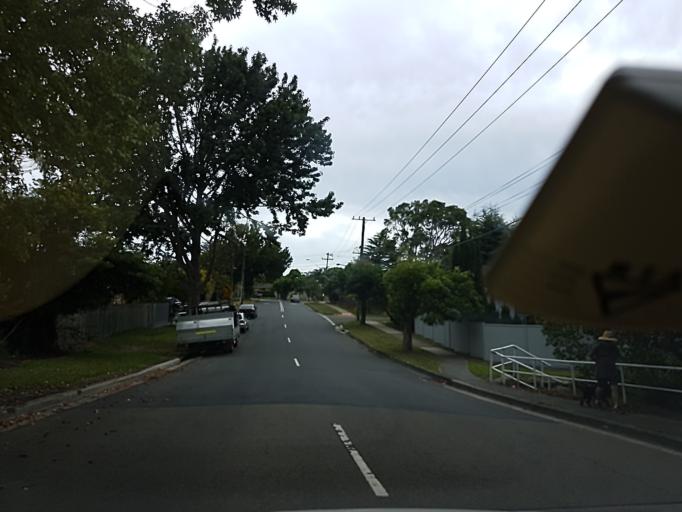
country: AU
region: New South Wales
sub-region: Warringah
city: Davidson
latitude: -33.7338
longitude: 151.2137
